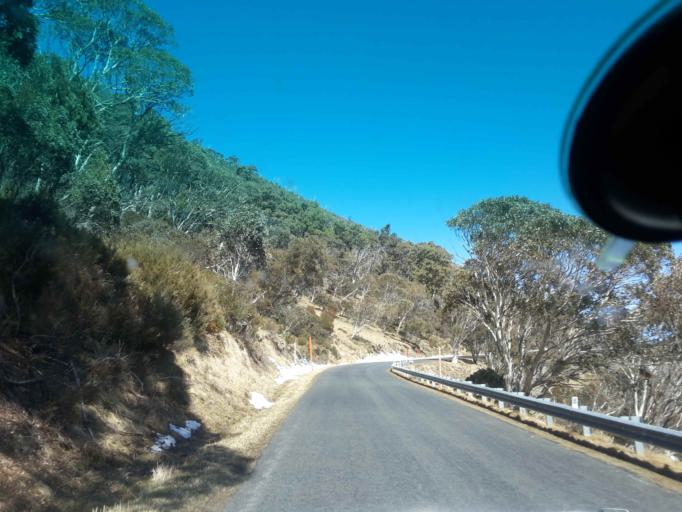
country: AU
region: New South Wales
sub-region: Snowy River
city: Jindabyne
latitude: -36.5155
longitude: 148.2868
